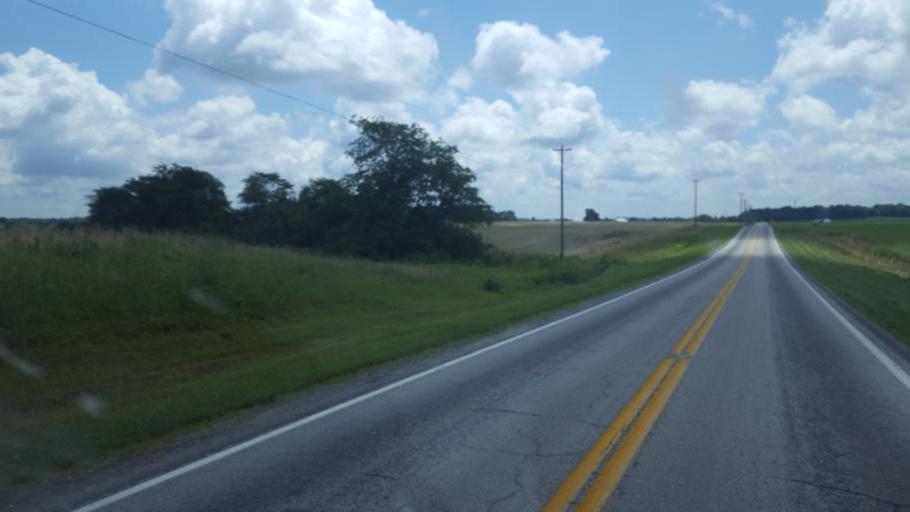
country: US
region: Ohio
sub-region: Highland County
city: Greenfield
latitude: 39.2507
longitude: -83.4404
